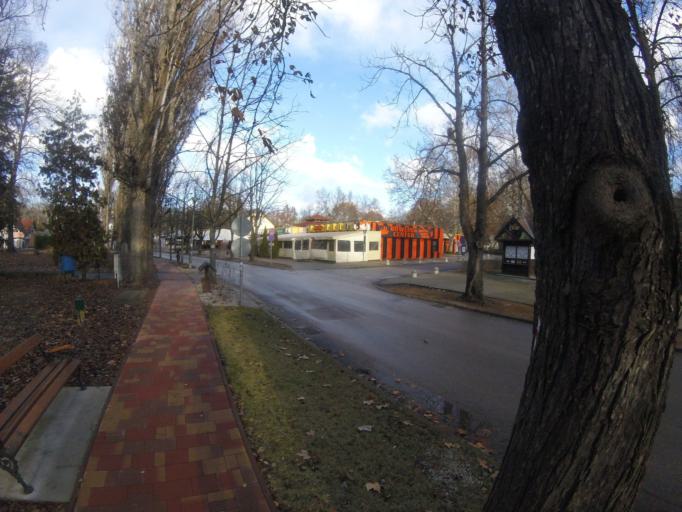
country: HU
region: Somogy
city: Balatonfoldvar
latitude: 46.8515
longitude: 17.8789
